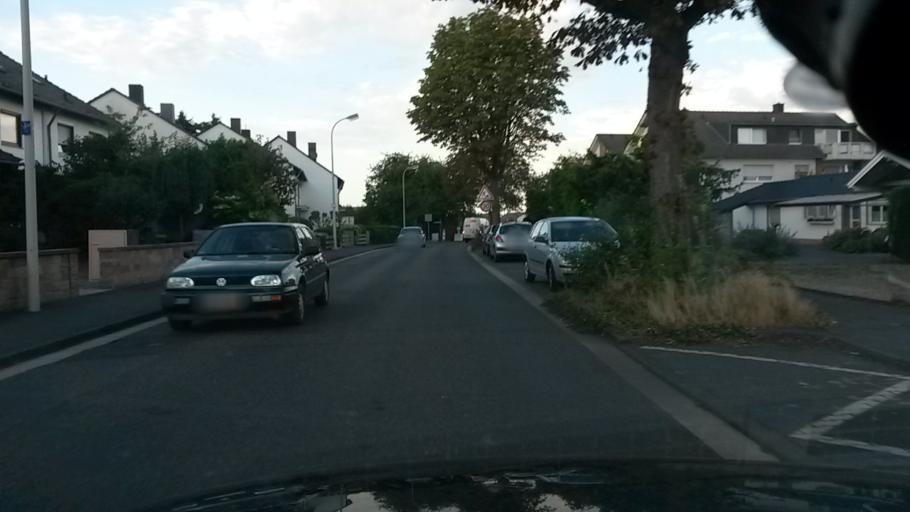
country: DE
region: North Rhine-Westphalia
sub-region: Regierungsbezirk Koln
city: Alfter
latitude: 50.7305
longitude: 7.0456
